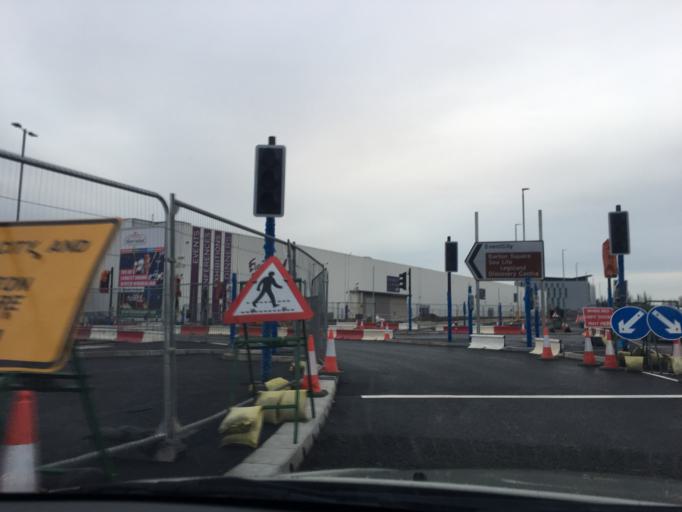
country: GB
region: England
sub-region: City and Borough of Salford
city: Eccles
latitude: 53.4655
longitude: -2.3419
